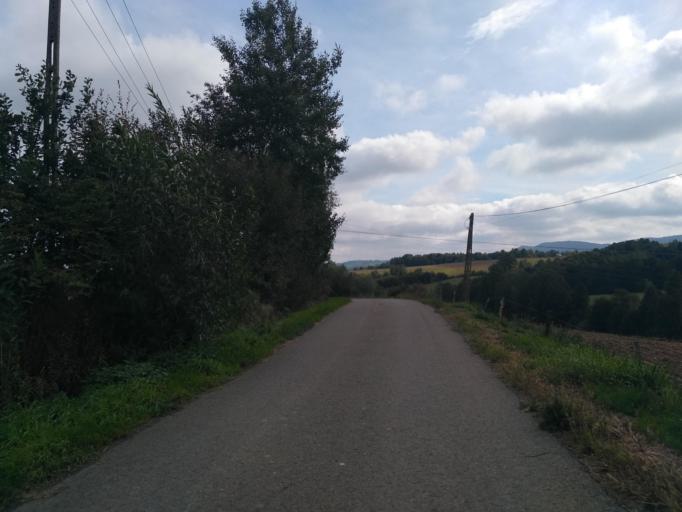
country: PL
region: Subcarpathian Voivodeship
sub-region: Powiat ropczycko-sedziszowski
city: Niedzwiada
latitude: 49.9416
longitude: 21.5158
